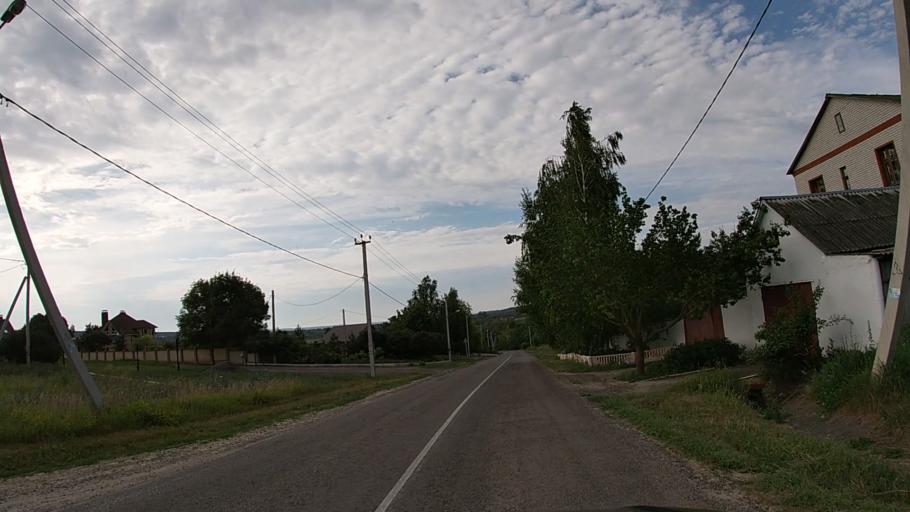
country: RU
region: Belgorod
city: Severnyy
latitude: 50.7139
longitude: 36.5950
